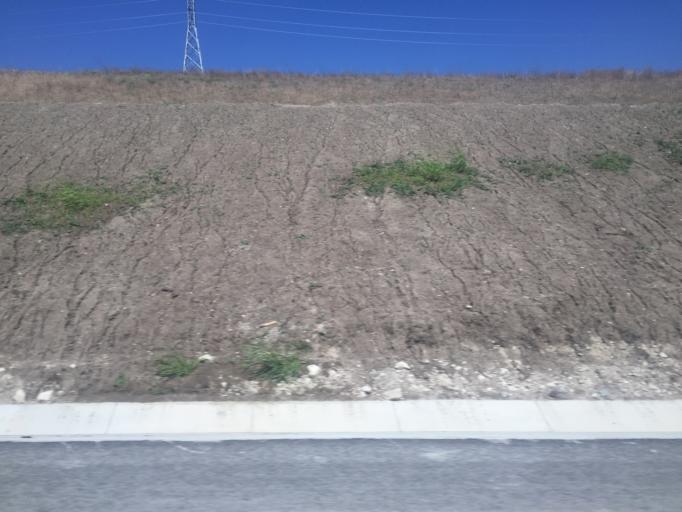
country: TR
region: Balikesir
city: Gobel
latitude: 39.9742
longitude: 28.1668
